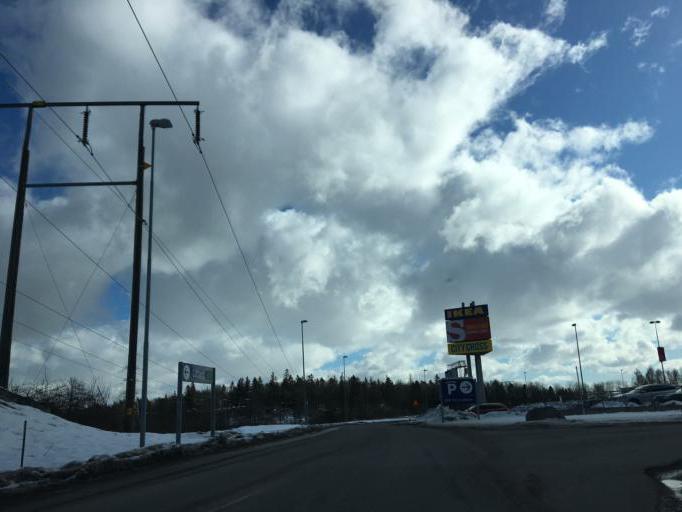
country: SE
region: Vaestmanland
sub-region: Vasteras
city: Vasteras
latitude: 59.6092
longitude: 16.4580
